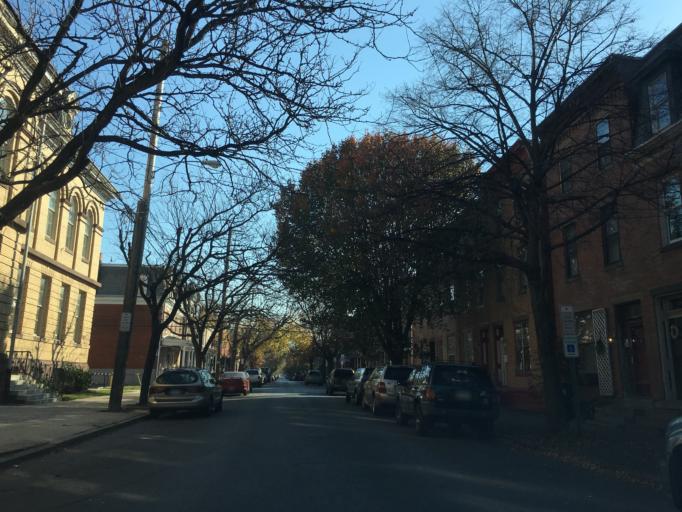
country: US
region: Pennsylvania
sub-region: Dauphin County
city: Harrisburg
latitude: 40.2757
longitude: -76.8950
